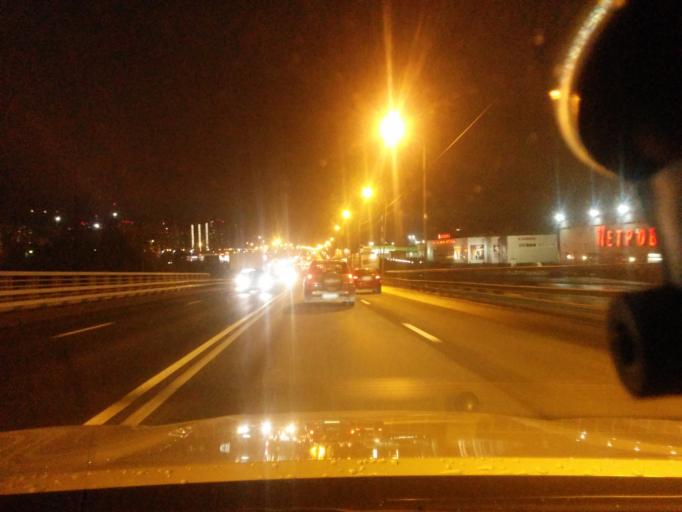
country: RU
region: Leningrad
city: Parnas
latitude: 60.0626
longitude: 30.3426
